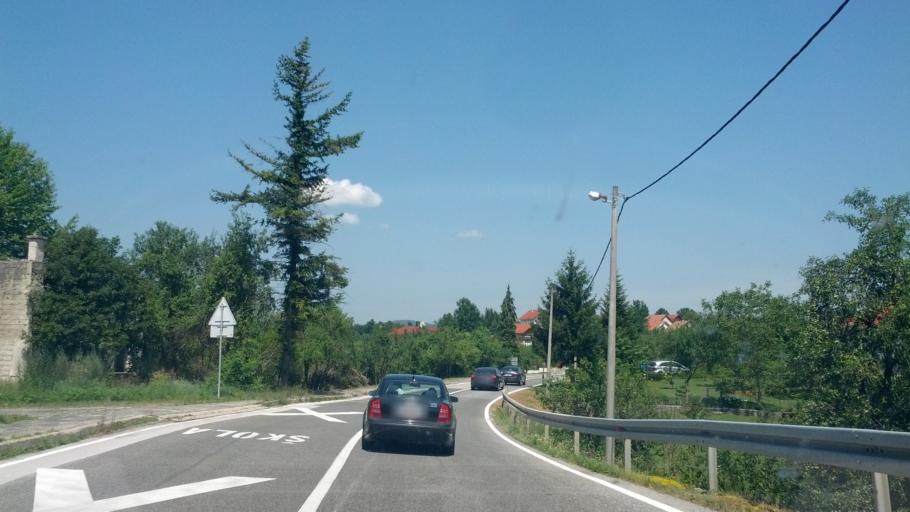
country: HR
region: Licko-Senjska
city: Jezerce
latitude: 44.9504
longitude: 15.6740
